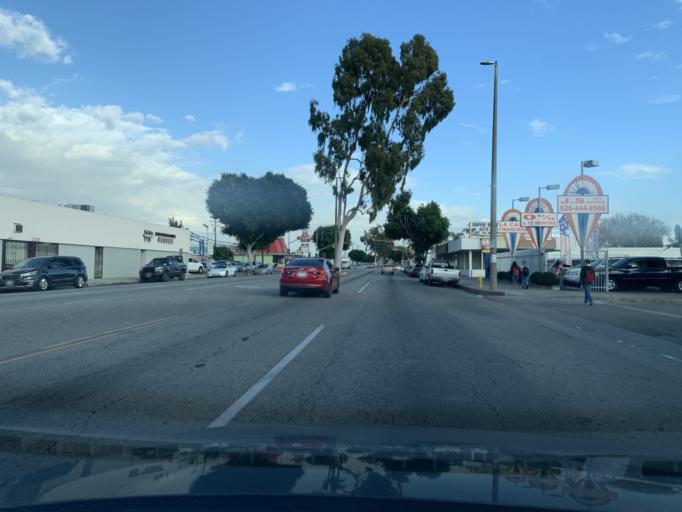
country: US
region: California
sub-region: Los Angeles County
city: El Monte
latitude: 34.0628
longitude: -118.0281
